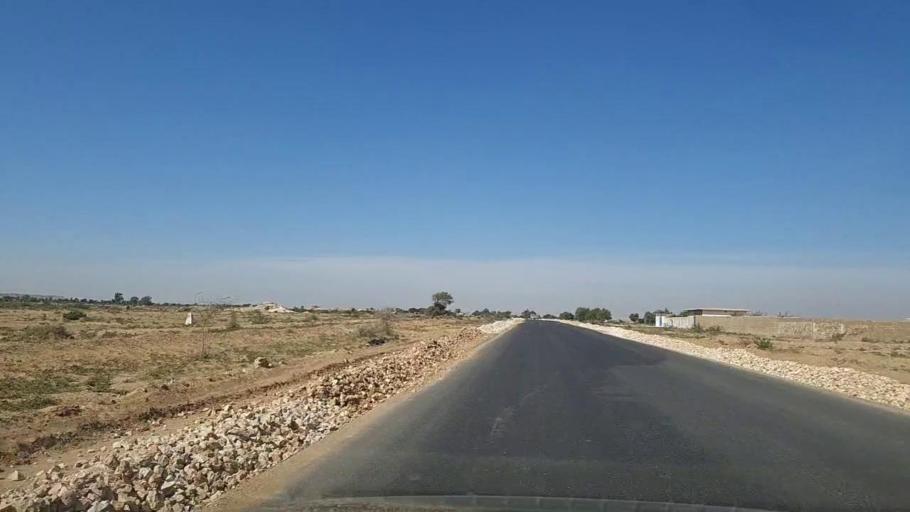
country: PK
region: Sindh
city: Kotri
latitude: 25.2785
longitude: 68.2132
